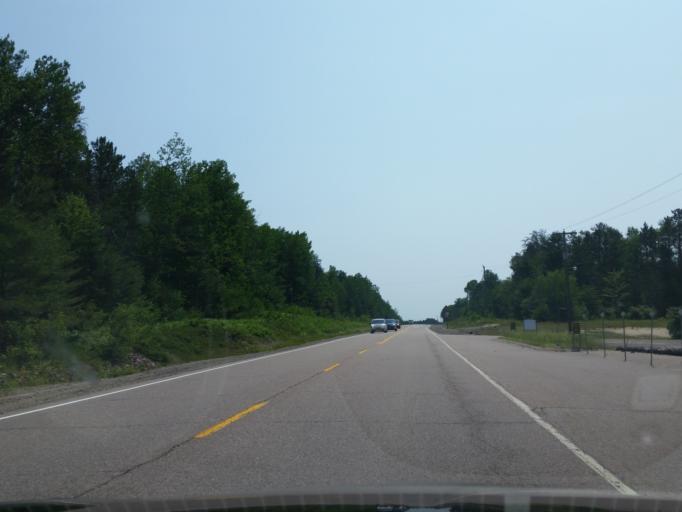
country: CA
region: Ontario
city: Deep River
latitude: 46.1862
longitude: -77.8637
